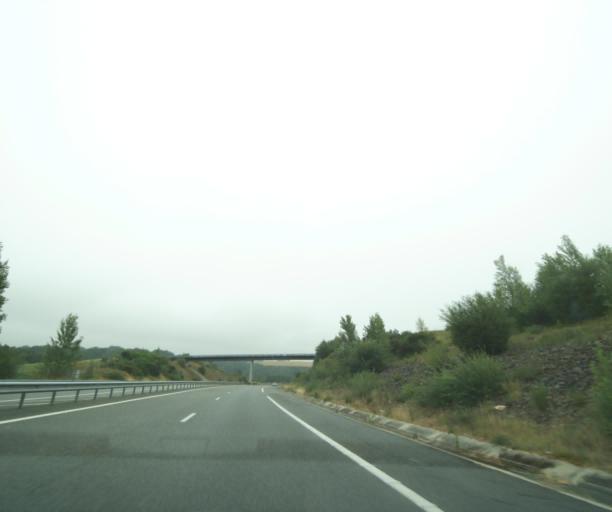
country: FR
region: Midi-Pyrenees
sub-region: Departement du Tarn
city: Carmaux
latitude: 44.0643
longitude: 2.2168
